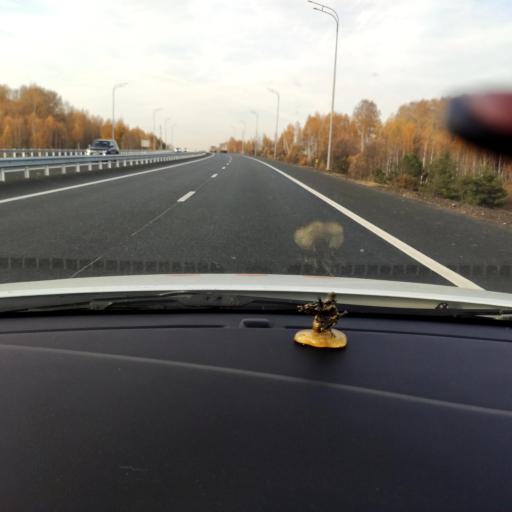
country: RU
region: Tatarstan
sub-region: Gorod Kazan'
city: Kazan
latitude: 55.9179
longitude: 49.1341
